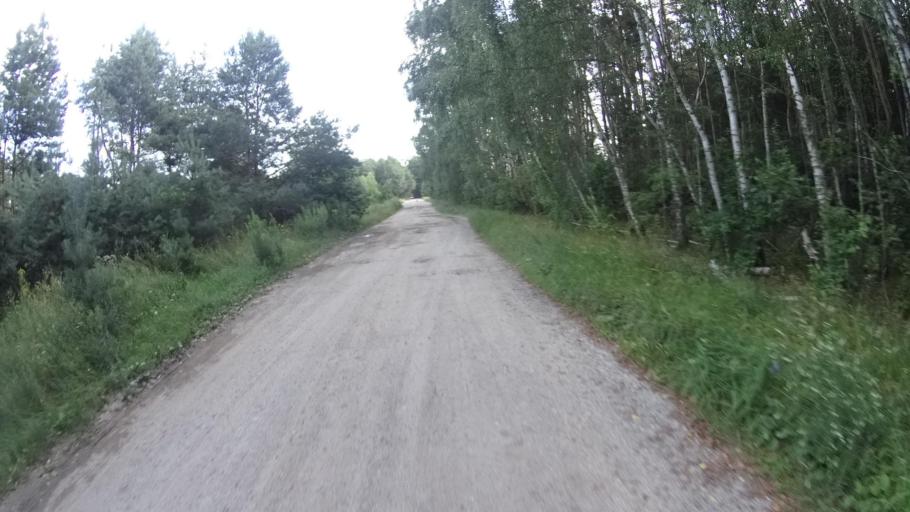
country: PL
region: Masovian Voivodeship
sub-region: Powiat piaseczynski
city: Tarczyn
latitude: 51.9695
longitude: 20.8540
